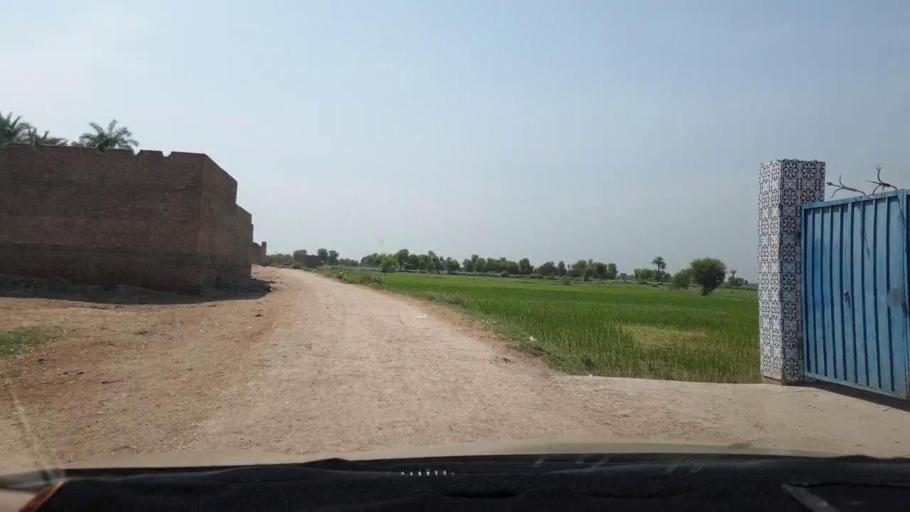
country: PK
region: Sindh
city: Naudero
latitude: 27.6474
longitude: 68.2740
